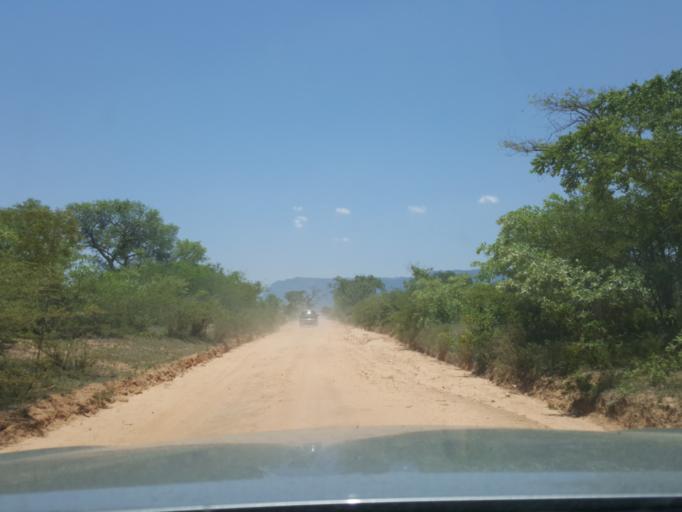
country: ZA
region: Limpopo
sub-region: Mopani District Municipality
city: Hoedspruit
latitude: -24.5794
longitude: 30.9917
